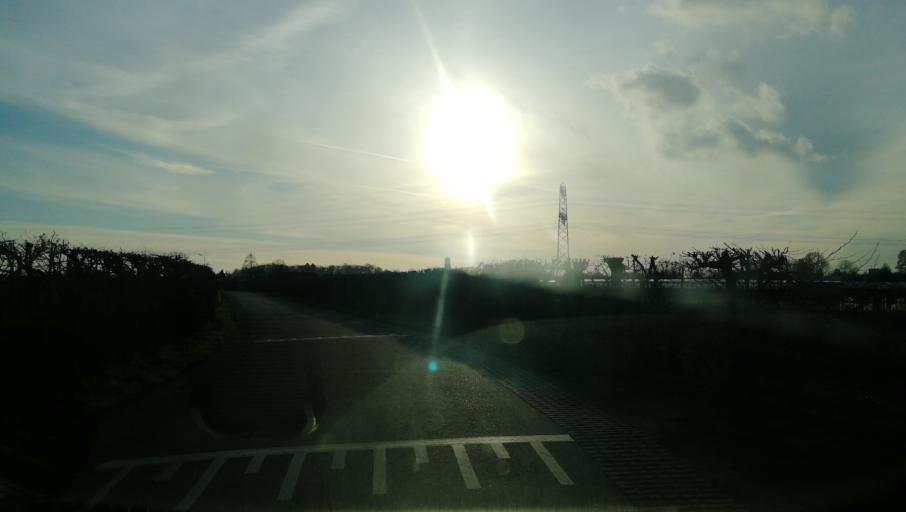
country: NL
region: Limburg
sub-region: Gemeente Venlo
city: Tegelen
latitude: 51.3395
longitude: 6.1063
